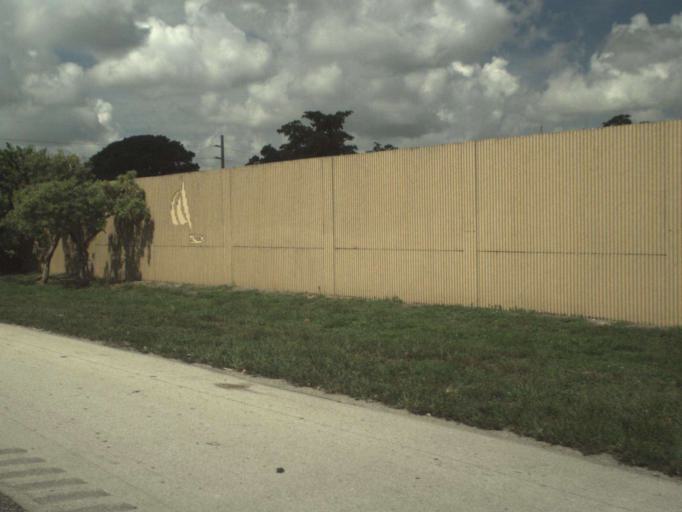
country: US
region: Florida
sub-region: Broward County
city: Tedder
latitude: 26.2912
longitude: -80.1237
